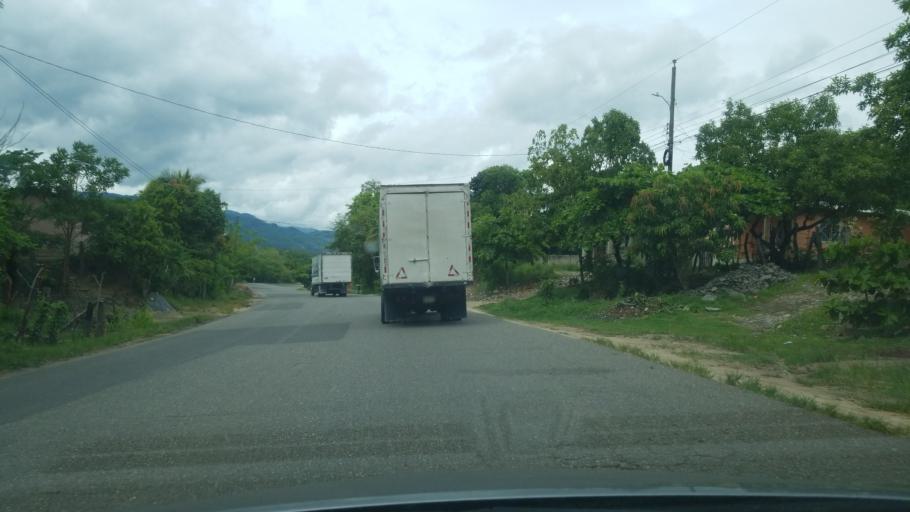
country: HN
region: Santa Barbara
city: San Marcos
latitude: 15.3116
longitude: -88.4394
